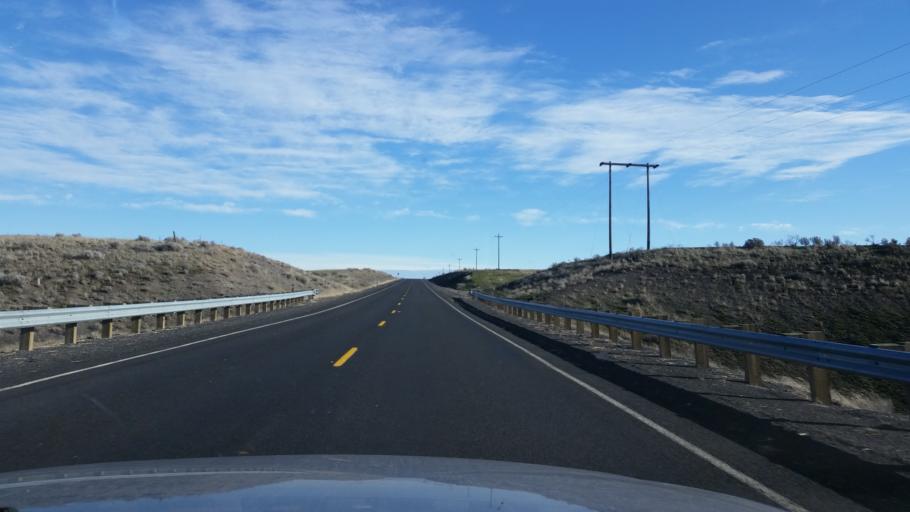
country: US
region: Washington
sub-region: Grant County
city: Warden
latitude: 47.3162
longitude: -118.8205
